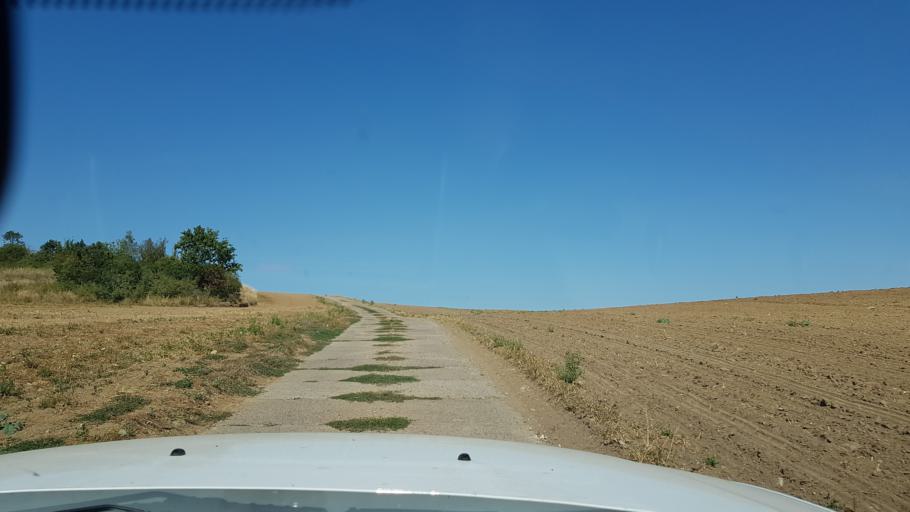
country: PL
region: West Pomeranian Voivodeship
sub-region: Powiat gryfinski
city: Moryn
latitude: 52.8512
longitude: 14.3592
